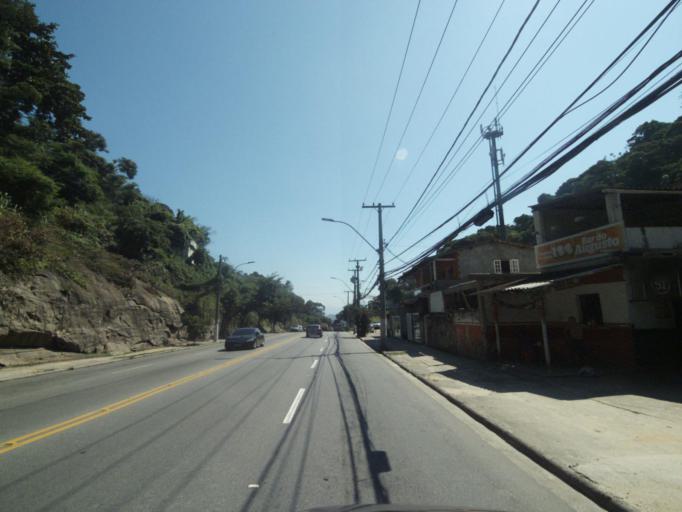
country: BR
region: Rio de Janeiro
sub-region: Niteroi
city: Niteroi
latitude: -22.9111
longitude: -43.0724
